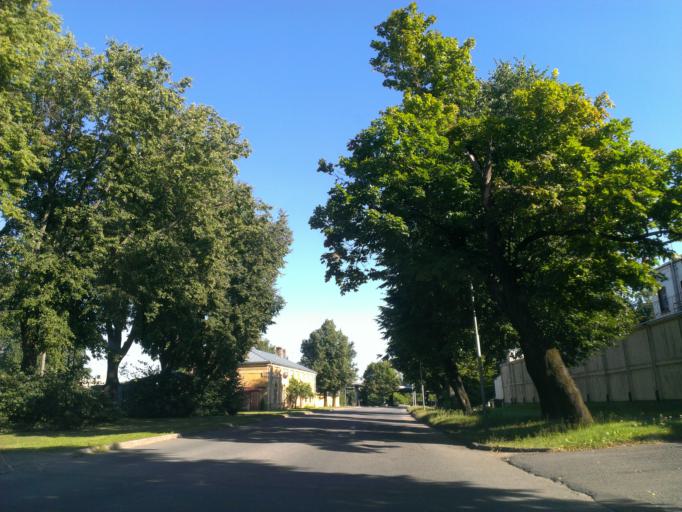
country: LV
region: Riga
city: Riga
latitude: 56.9794
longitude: 24.1437
